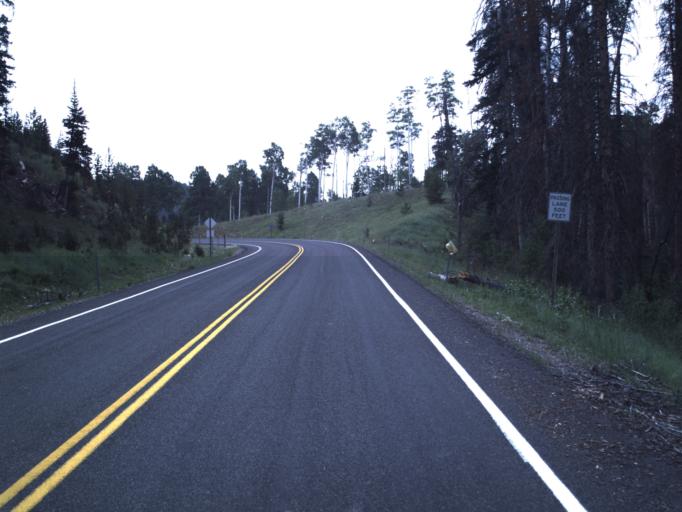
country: US
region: Utah
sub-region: Summit County
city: Francis
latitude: 40.5170
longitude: -111.0474
